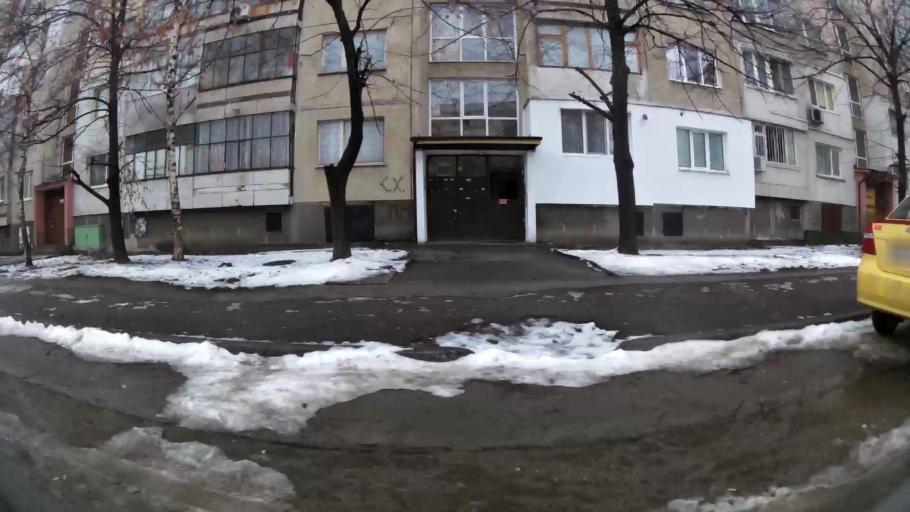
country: BG
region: Sofia-Capital
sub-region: Stolichna Obshtina
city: Sofia
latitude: 42.7104
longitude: 23.2606
